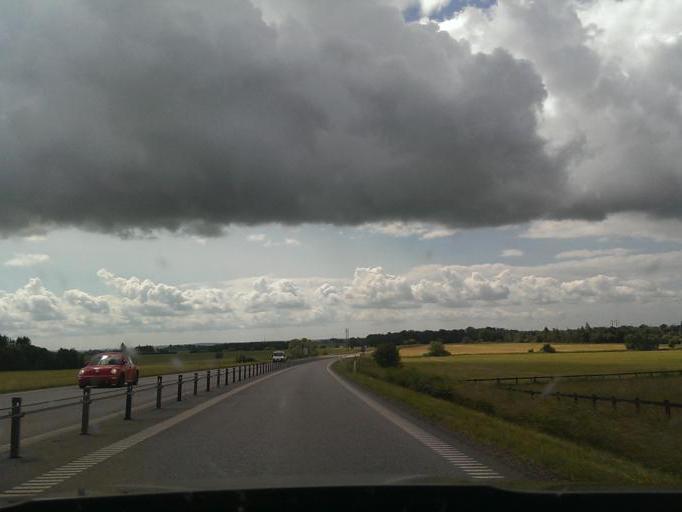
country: SE
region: Skane
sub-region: Eslovs Kommun
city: Eslov
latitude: 55.8215
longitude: 13.3359
